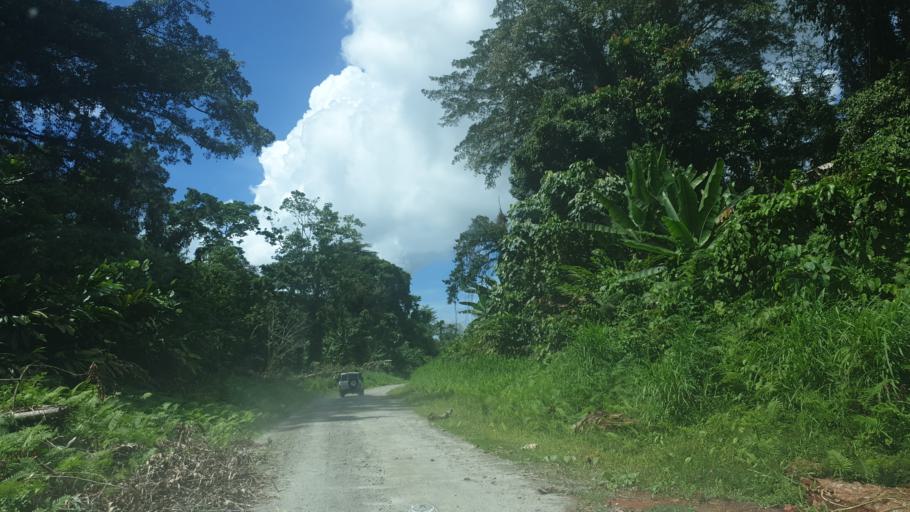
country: PG
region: Bougainville
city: Panguna
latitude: -6.7356
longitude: 155.4982
